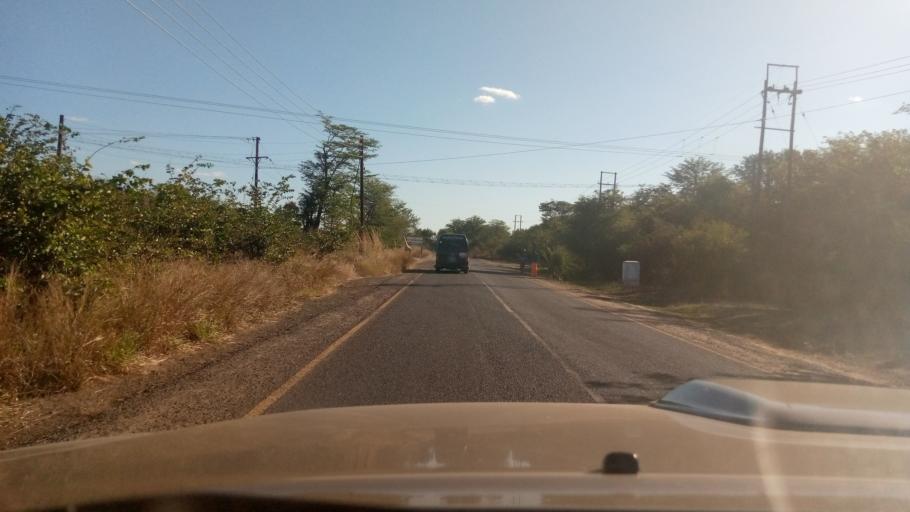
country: ZM
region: Southern
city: Livingstone
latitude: -17.8779
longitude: 25.8521
